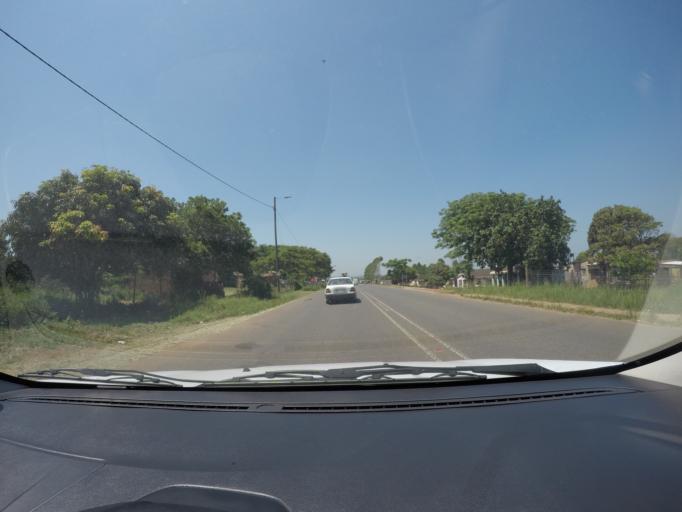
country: ZA
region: KwaZulu-Natal
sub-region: uThungulu District Municipality
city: eSikhawini
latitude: -28.8243
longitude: 31.9463
